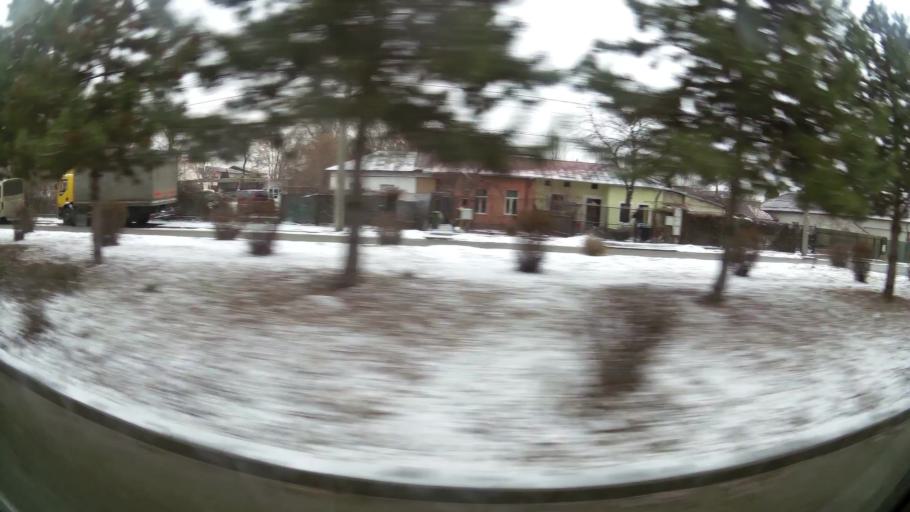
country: RO
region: Prahova
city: Ploiesti
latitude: 44.9329
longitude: 26.0511
